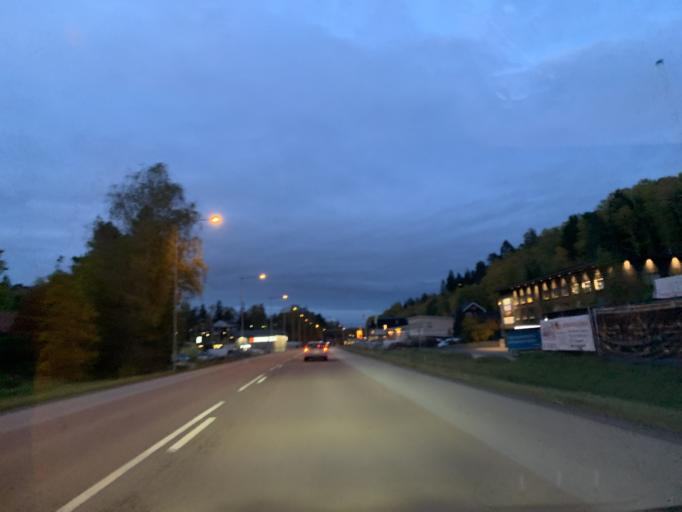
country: SE
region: Stockholm
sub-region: Botkyrka Kommun
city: Tumba
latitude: 59.1939
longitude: 17.8271
